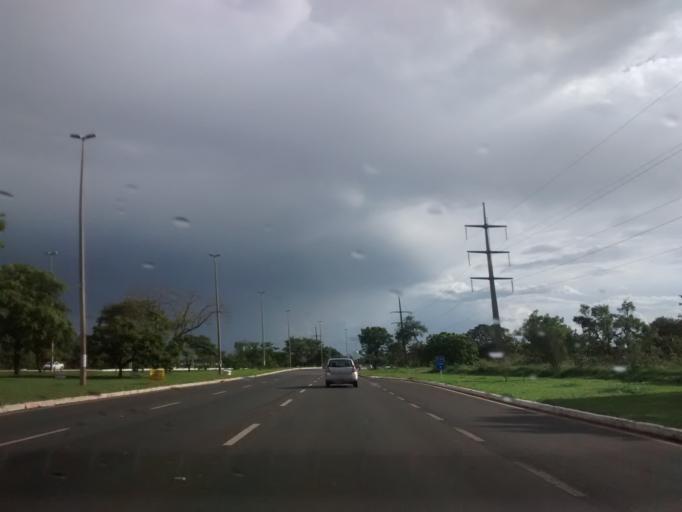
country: BR
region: Federal District
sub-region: Brasilia
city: Brasilia
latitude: -15.7712
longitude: -47.8639
